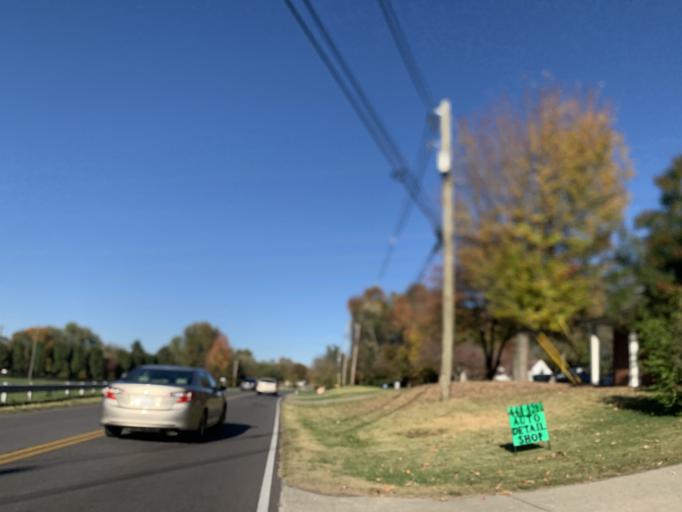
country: US
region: Kentucky
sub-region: Jefferson County
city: Saint Dennis
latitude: 38.1654
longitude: -85.8424
